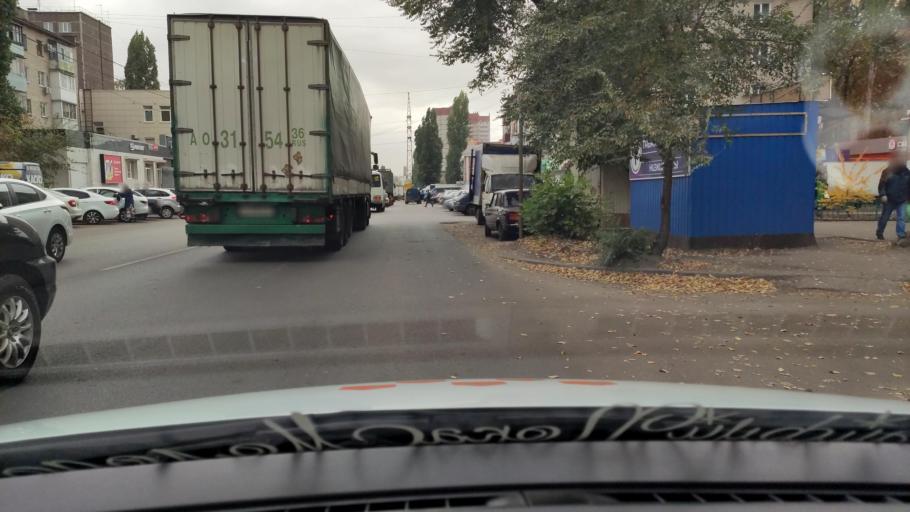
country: RU
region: Voronezj
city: Voronezh
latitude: 51.6750
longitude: 39.1564
